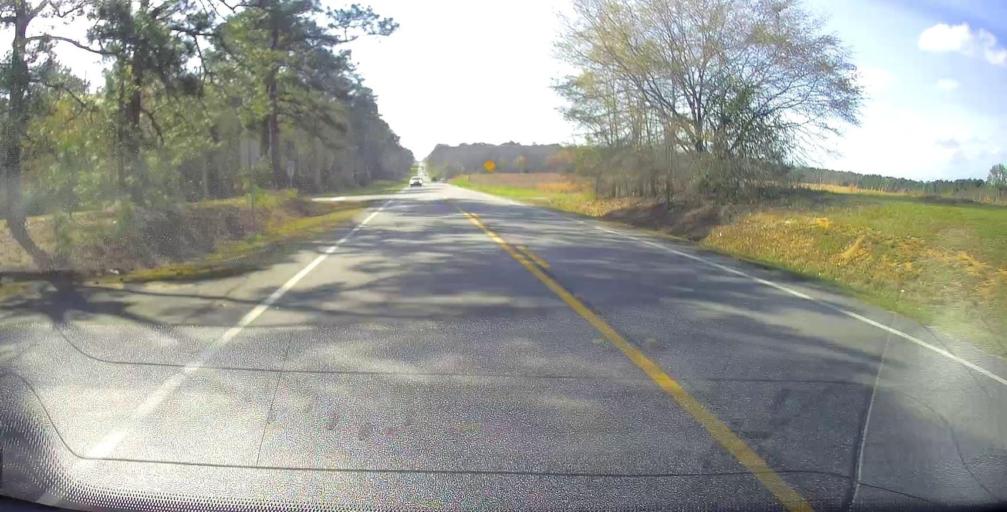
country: US
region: Georgia
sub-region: Dodge County
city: Eastman
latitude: 32.1964
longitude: -83.1911
